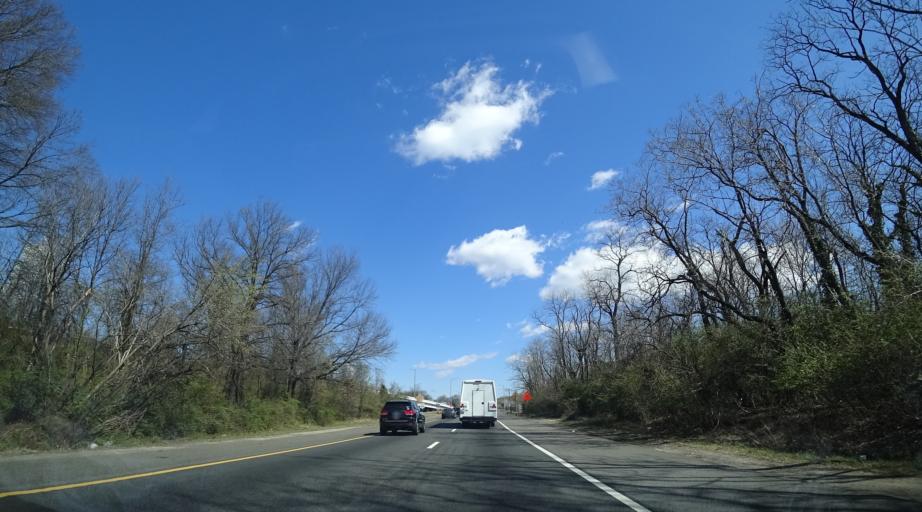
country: US
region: Maryland
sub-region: Prince George's County
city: Coral Hills
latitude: 38.8882
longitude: -76.9608
